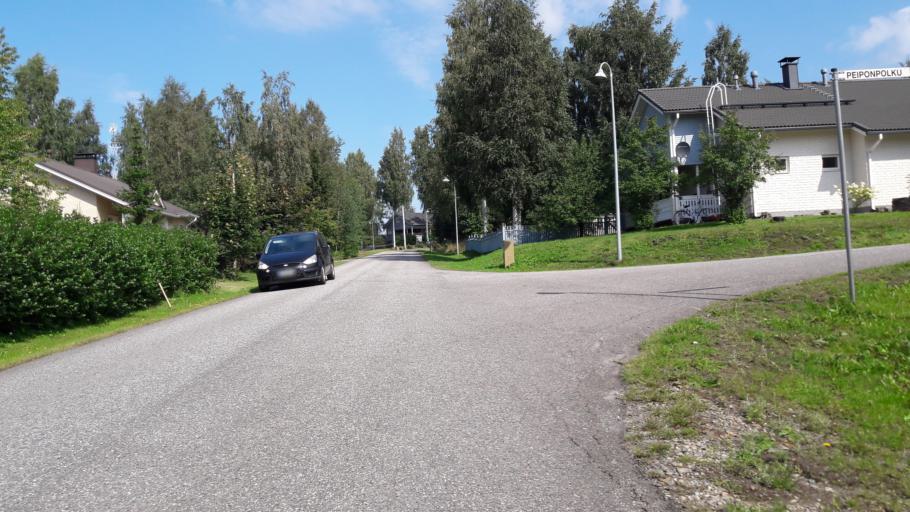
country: FI
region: North Karelia
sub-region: Joensuu
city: Joensuu
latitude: 62.5264
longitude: 29.8407
